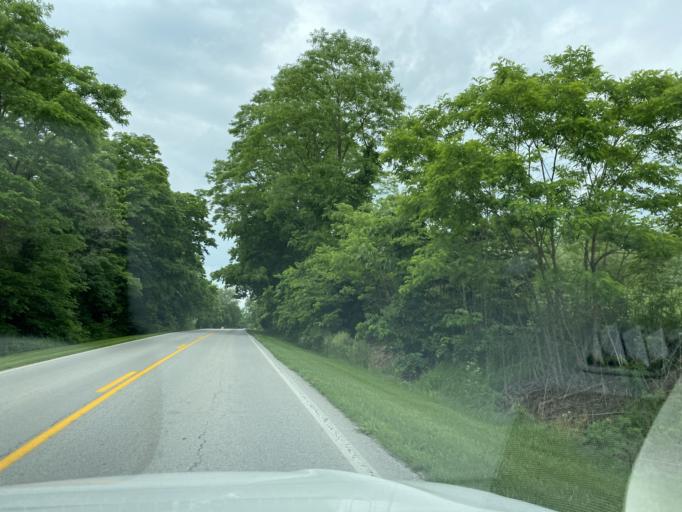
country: US
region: Kentucky
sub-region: Scott County
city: Georgetown
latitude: 38.2202
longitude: -84.5032
